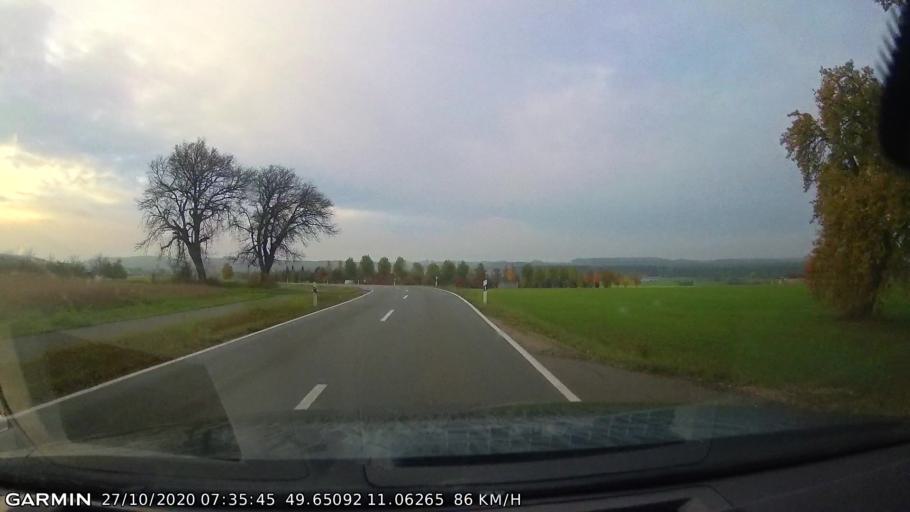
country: DE
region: Bavaria
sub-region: Upper Franconia
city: Langensendelbach
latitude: 49.6507
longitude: 11.0627
